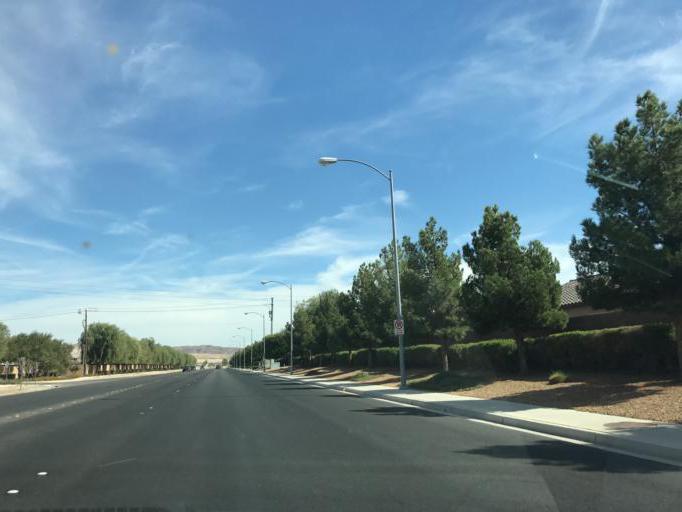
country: US
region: Nevada
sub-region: Clark County
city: Whitney
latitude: 36.1297
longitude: -115.0439
